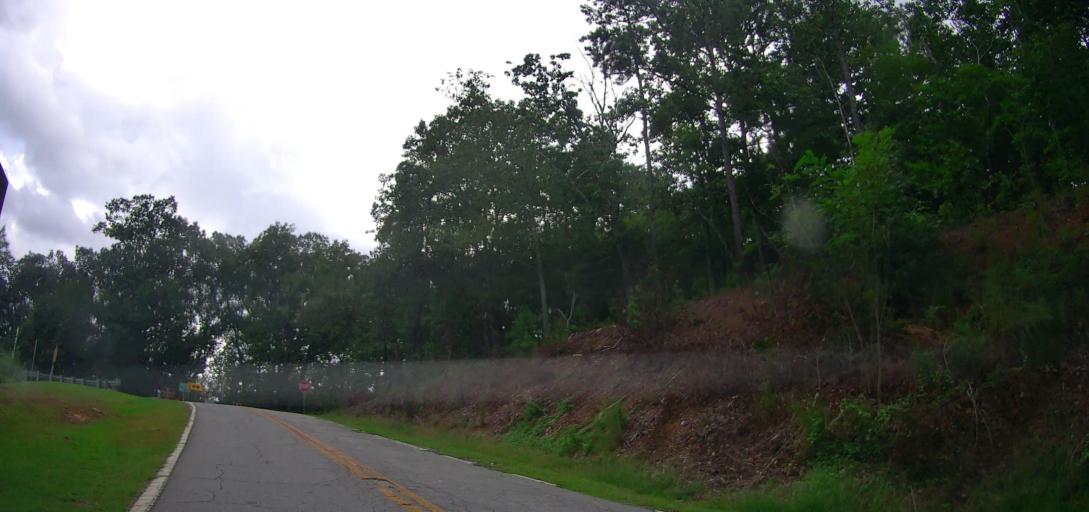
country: US
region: Georgia
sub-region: Harris County
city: Pine Mountain
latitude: 32.8412
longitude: -84.8093
